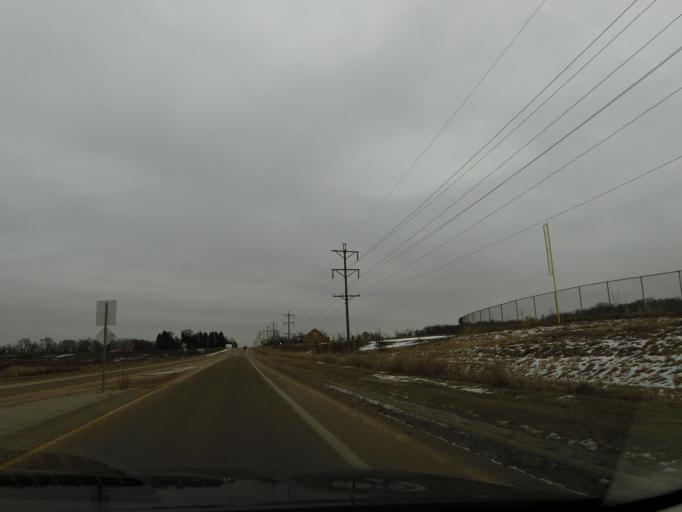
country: US
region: Minnesota
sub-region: Carver County
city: Watertown
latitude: 44.9631
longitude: -93.8275
